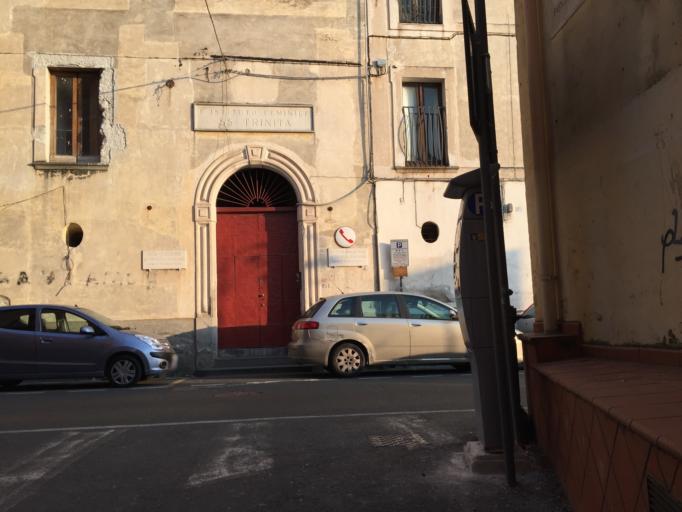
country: IT
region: Campania
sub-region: Provincia di Napoli
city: Vico Equense
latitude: 40.6632
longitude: 14.4242
